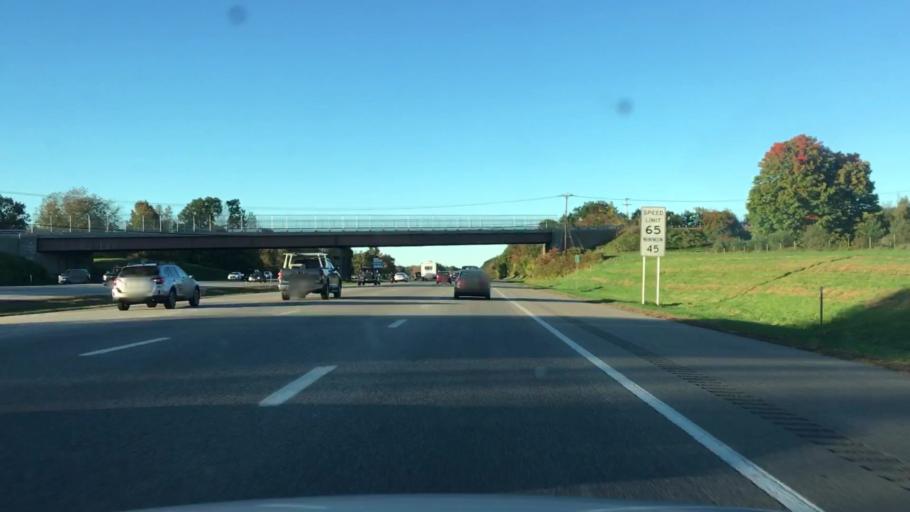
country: US
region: New Hampshire
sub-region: Rockingham County
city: North Hampton
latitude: 42.9733
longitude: -70.8539
